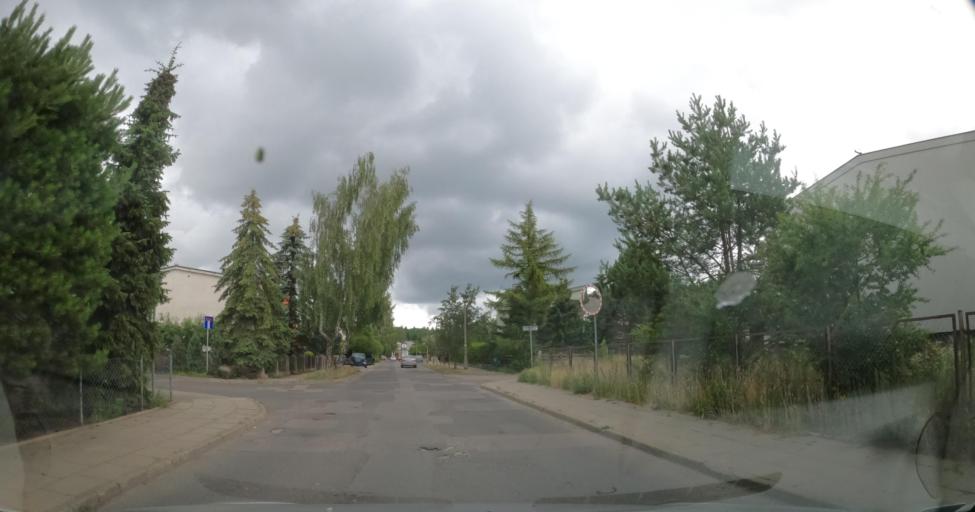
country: PL
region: Pomeranian Voivodeship
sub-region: Gdynia
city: Wielki Kack
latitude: 54.4285
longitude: 18.4741
